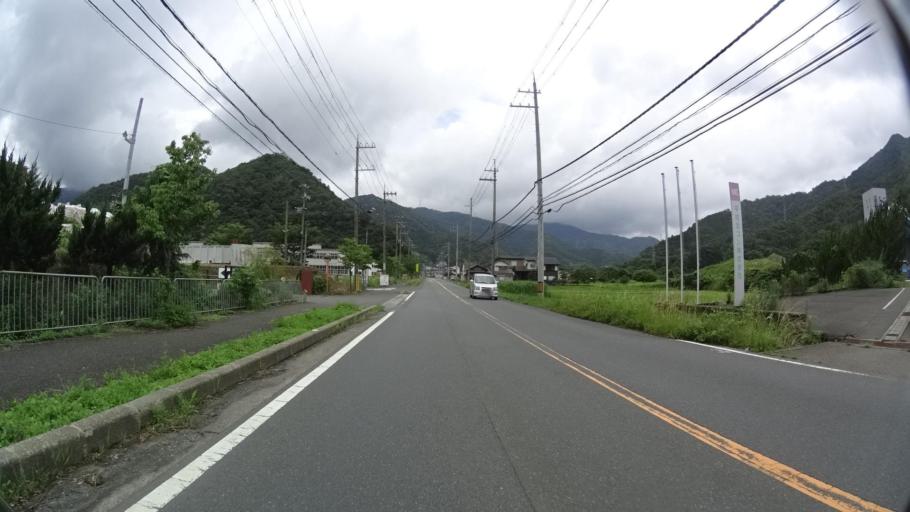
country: JP
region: Kyoto
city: Maizuru
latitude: 35.5045
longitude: 135.3812
